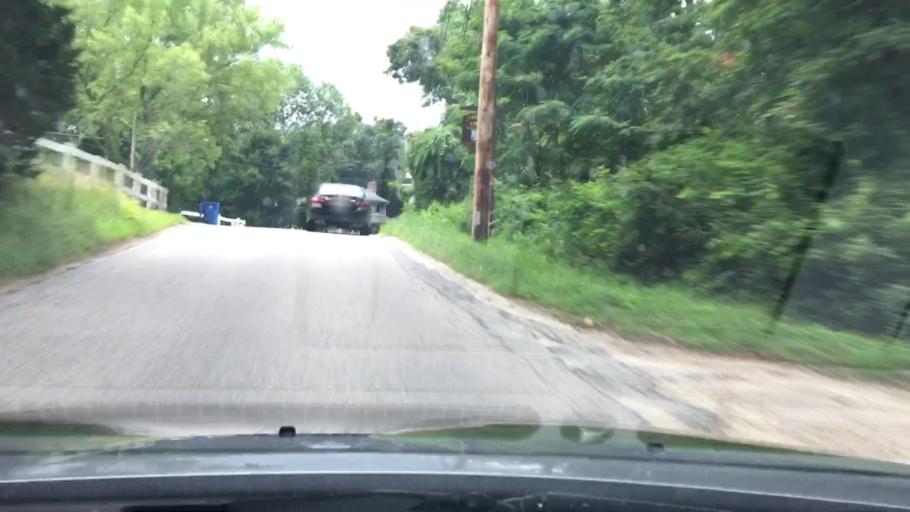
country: US
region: Rhode Island
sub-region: Providence County
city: Cumberland Hill
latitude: 42.0132
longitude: -71.4463
